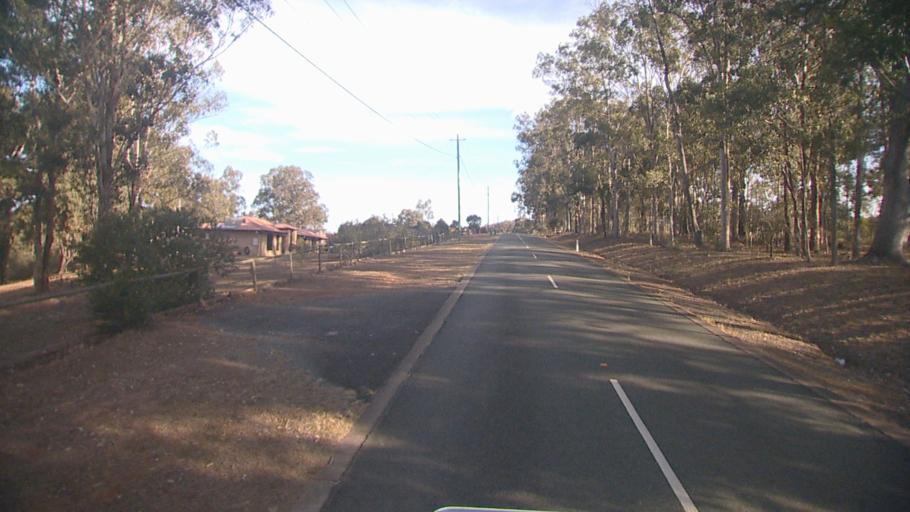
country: AU
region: Queensland
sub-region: Logan
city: Cedar Vale
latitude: -27.8824
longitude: 153.0102
